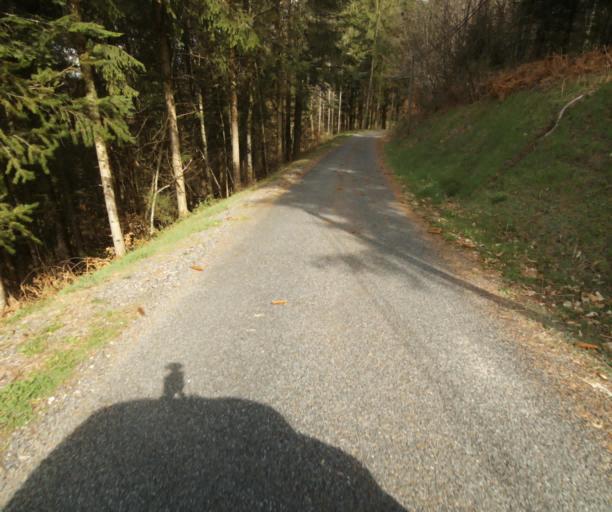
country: FR
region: Limousin
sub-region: Departement de la Correze
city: Correze
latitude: 45.3545
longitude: 1.8802
